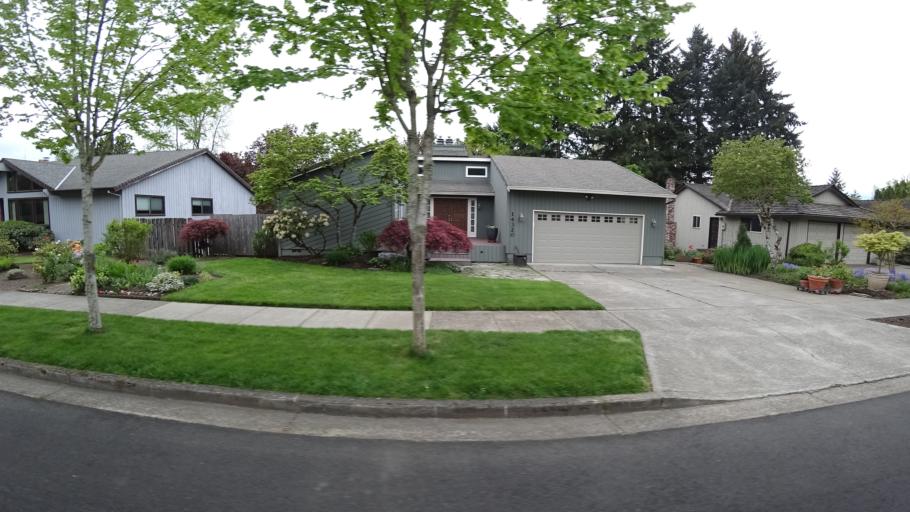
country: US
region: Oregon
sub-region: Washington County
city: Beaverton
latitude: 45.4545
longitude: -122.8243
